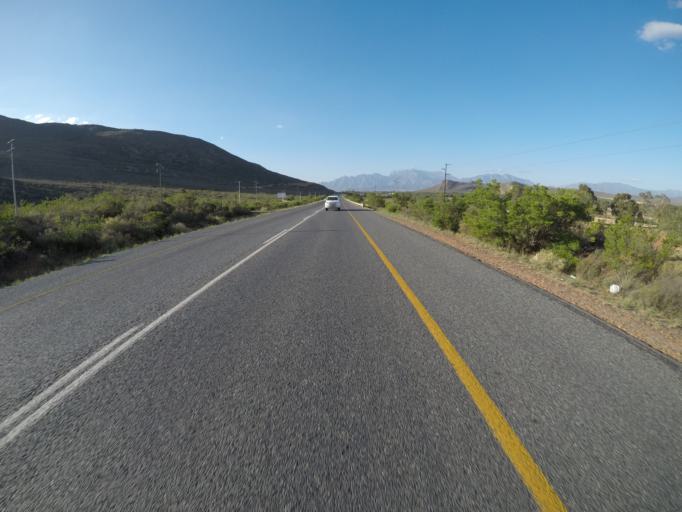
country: ZA
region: Western Cape
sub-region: Cape Winelands District Municipality
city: Worcester
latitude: -33.7502
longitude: 19.4811
